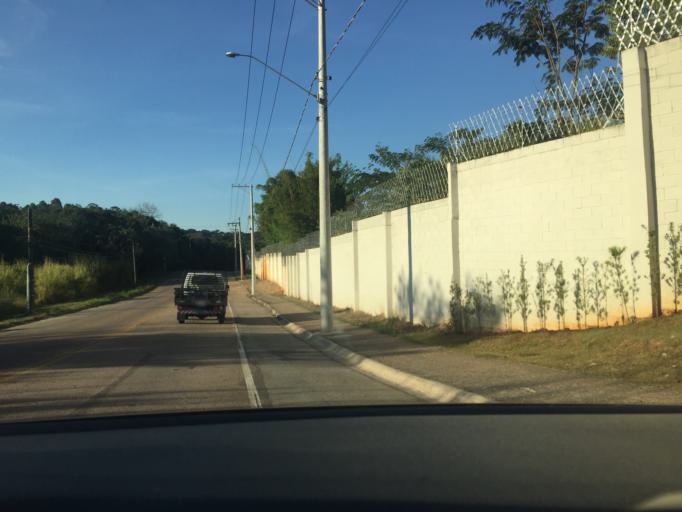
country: BR
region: Sao Paulo
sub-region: Louveira
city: Louveira
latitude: -23.1219
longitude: -46.9281
